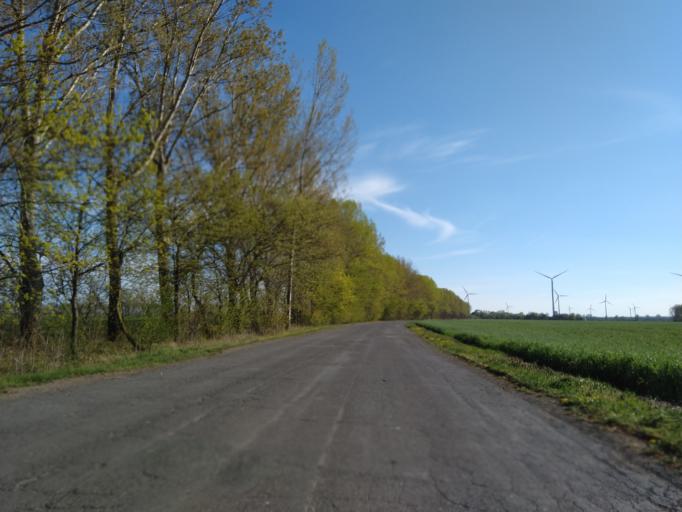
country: DE
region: Brandenburg
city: Neutrebbin
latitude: 52.7253
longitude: 14.2142
